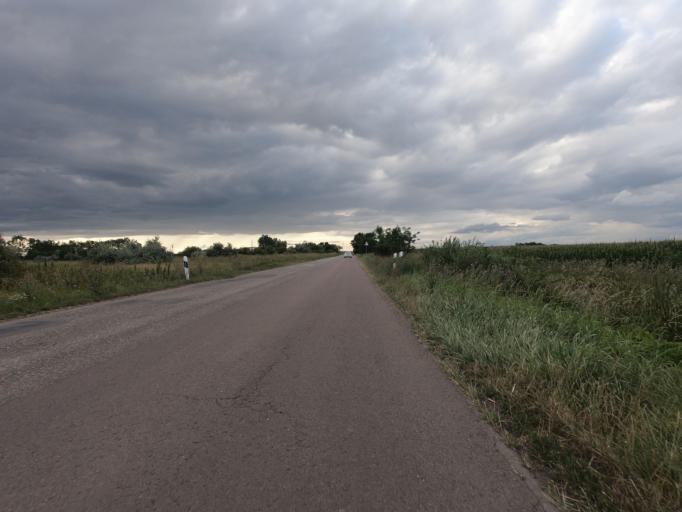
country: HU
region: Heves
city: Poroszlo
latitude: 47.6771
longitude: 20.6545
